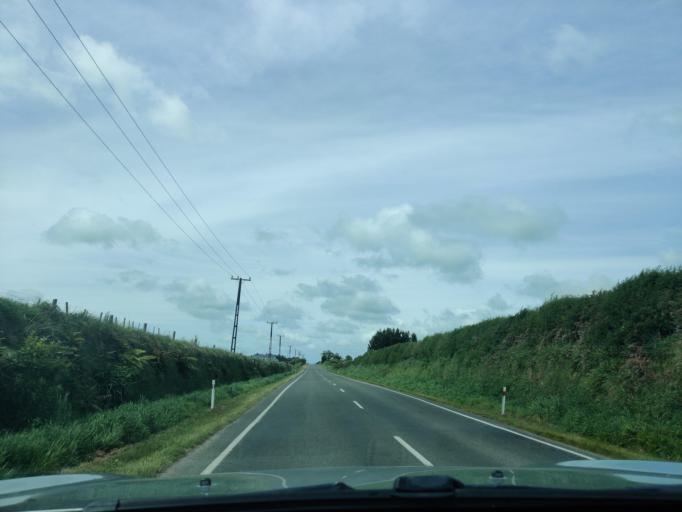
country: NZ
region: Taranaki
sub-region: South Taranaki District
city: Eltham
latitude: -39.4282
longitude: 174.1620
